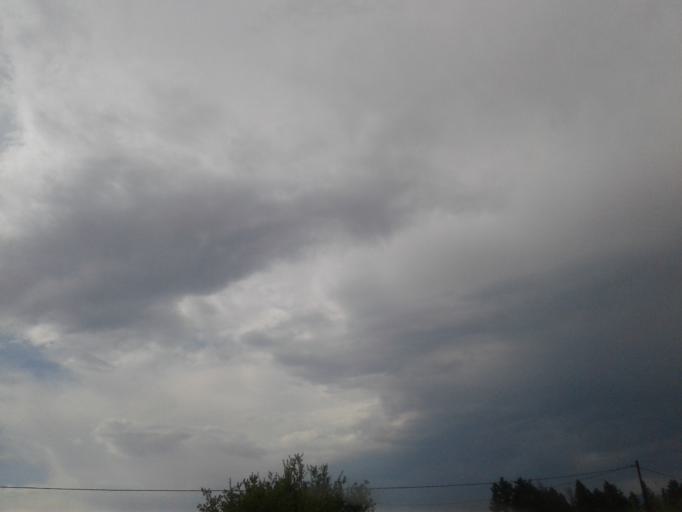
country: LS
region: Quthing
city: Quthing
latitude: -30.3810
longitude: 27.5545
